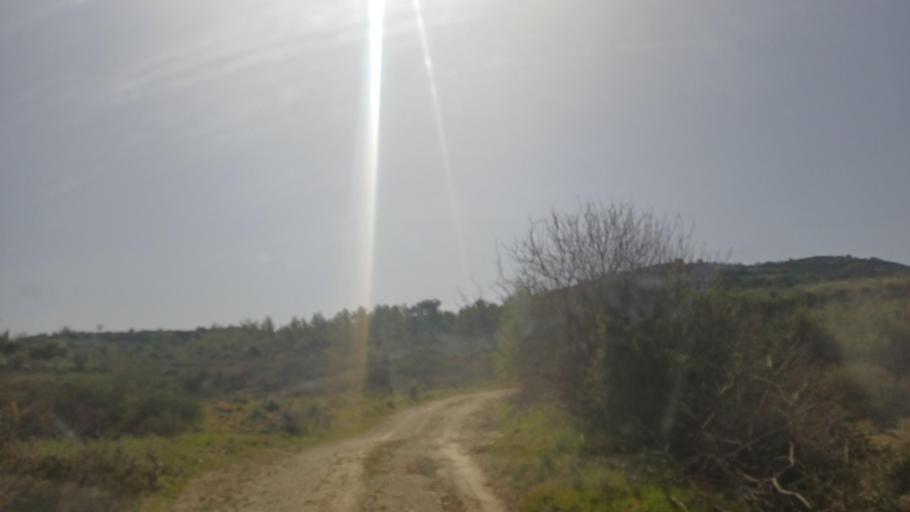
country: CY
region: Limassol
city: Pachna
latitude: 34.8769
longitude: 32.7005
